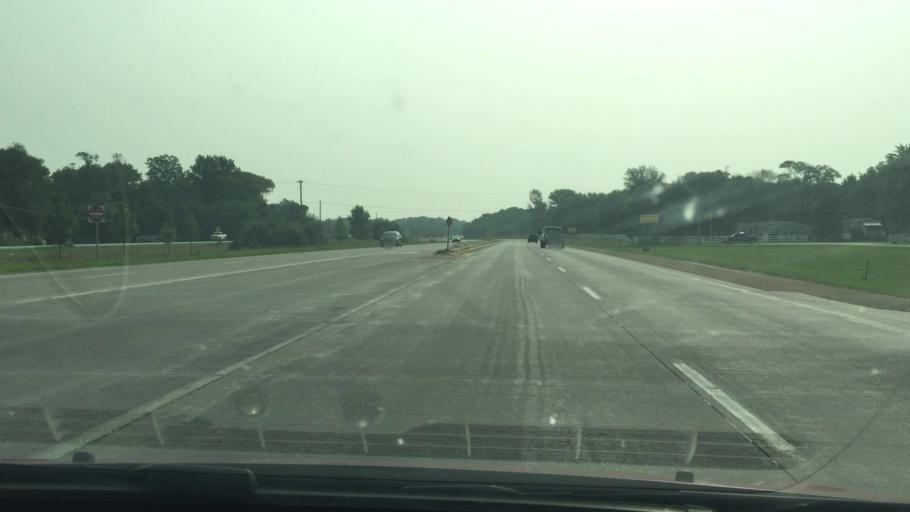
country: US
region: Iowa
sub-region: Scott County
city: Buffalo
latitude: 41.5085
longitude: -90.6841
